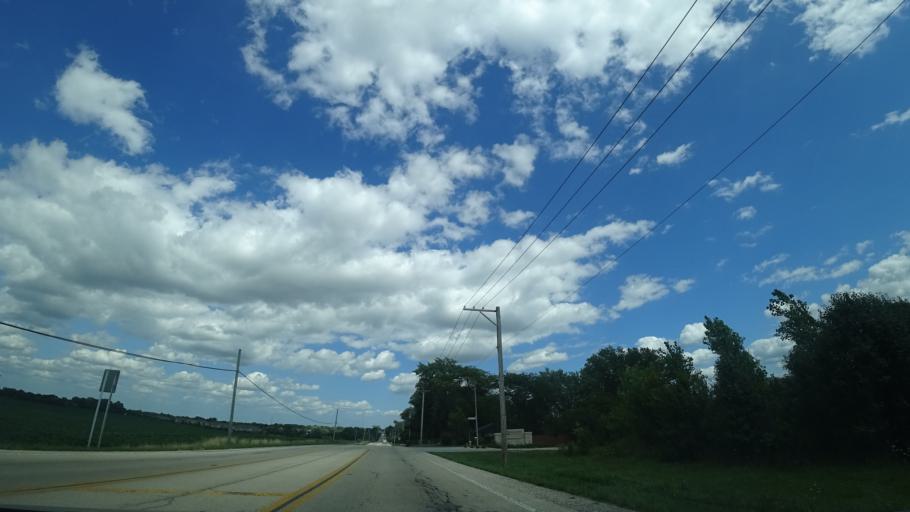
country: US
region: Illinois
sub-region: Will County
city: Homer Glen
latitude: 41.5860
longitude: -87.8984
